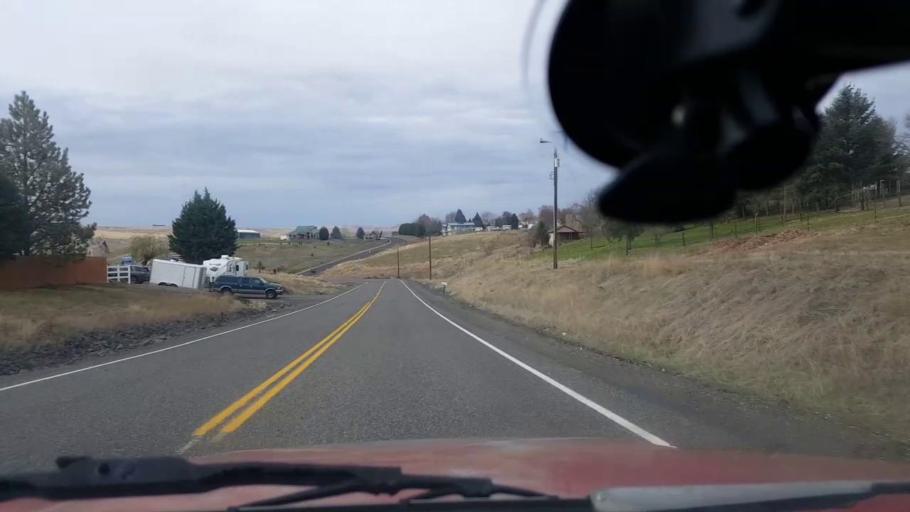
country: US
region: Washington
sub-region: Asotin County
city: Clarkston Heights-Vineland
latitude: 46.4019
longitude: -117.0851
